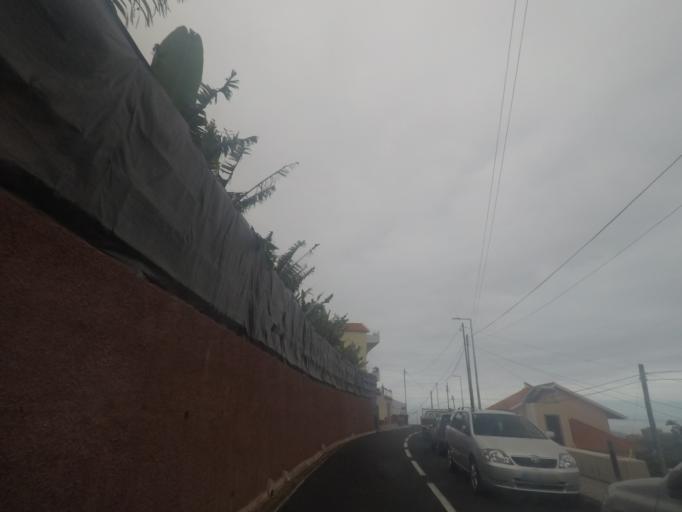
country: PT
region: Madeira
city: Camara de Lobos
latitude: 32.6632
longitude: -16.9712
